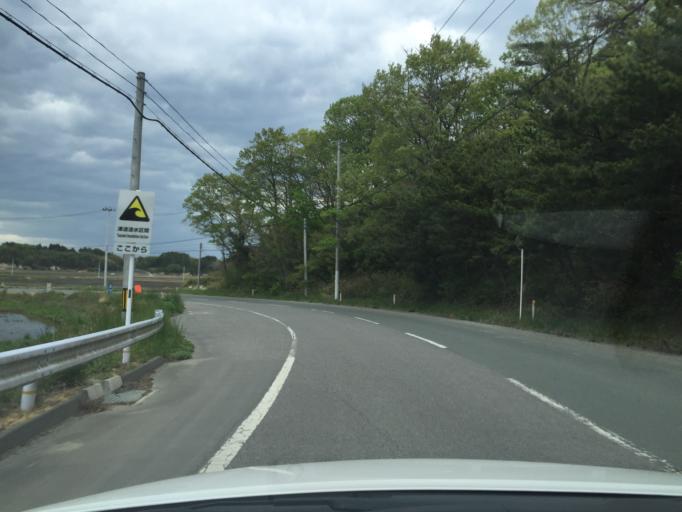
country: JP
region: Fukushima
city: Namie
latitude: 37.7523
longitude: 140.9991
